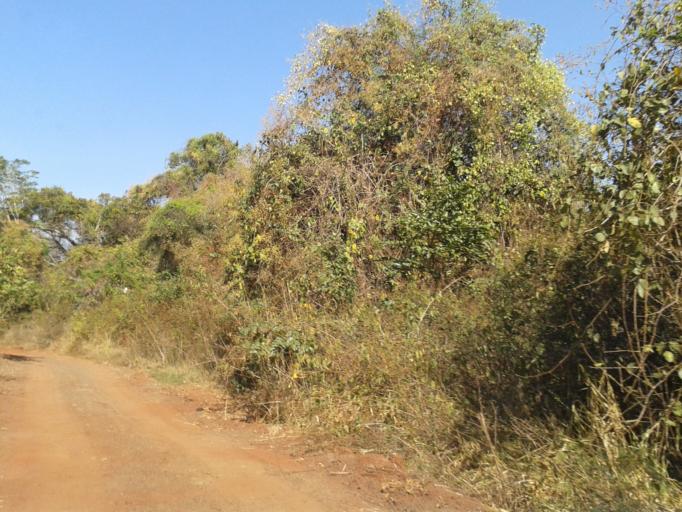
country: BR
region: Minas Gerais
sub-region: Santa Vitoria
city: Santa Vitoria
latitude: -19.2081
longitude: -50.0365
